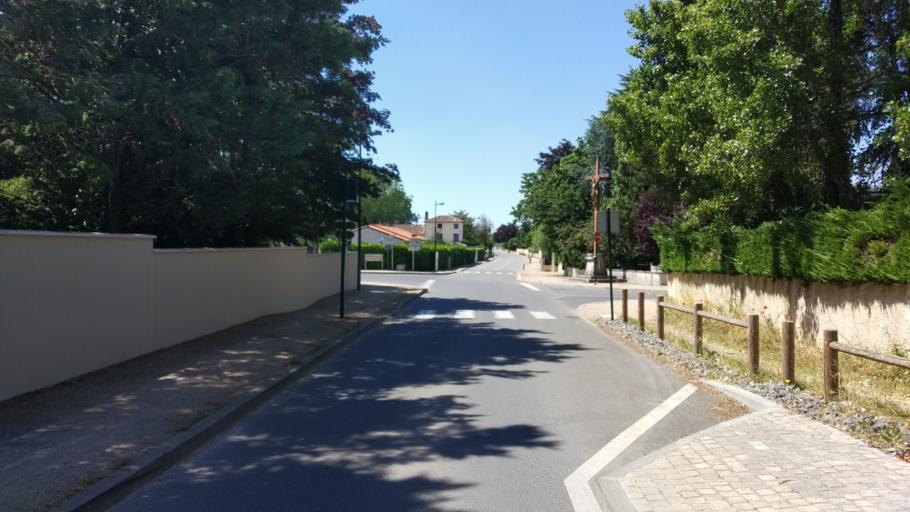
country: FR
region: Poitou-Charentes
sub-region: Departement de la Vienne
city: Vouneuil-sous-Biard
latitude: 46.6032
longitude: 0.2831
